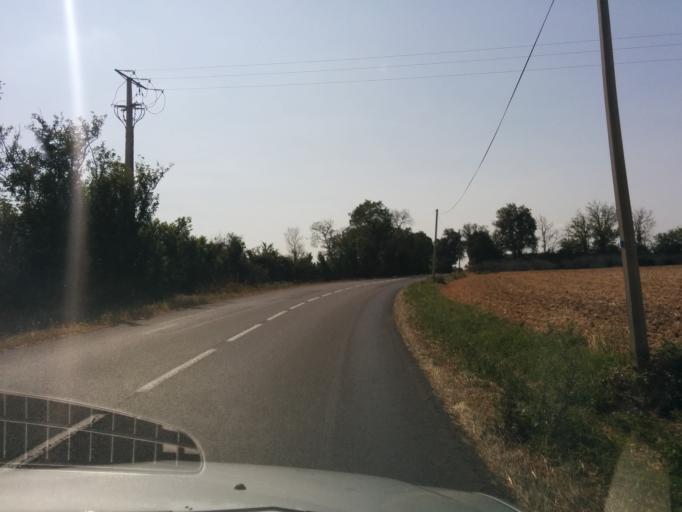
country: FR
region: Poitou-Charentes
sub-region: Departement de la Vienne
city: Saint-Jean-de-Sauves
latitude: 46.8026
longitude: 0.0791
